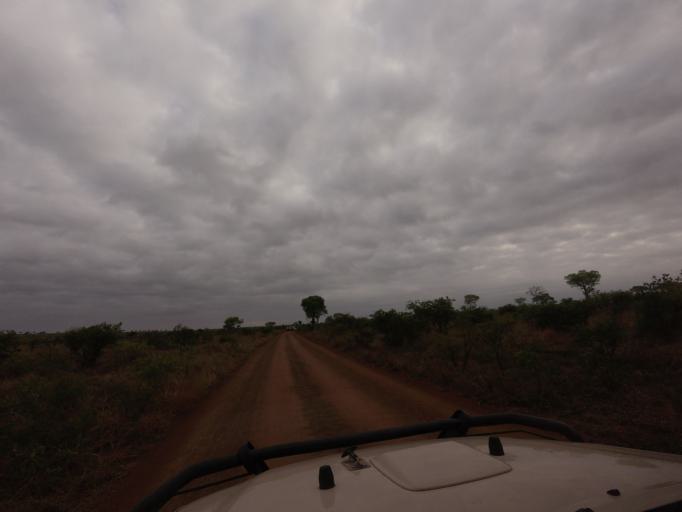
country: ZA
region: Mpumalanga
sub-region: Ehlanzeni District
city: Komatipoort
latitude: -25.2962
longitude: 31.9215
